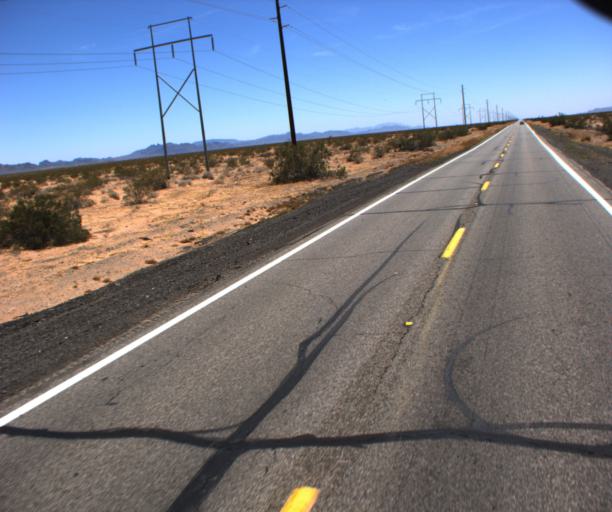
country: US
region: Arizona
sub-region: La Paz County
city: Quartzsite
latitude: 33.9048
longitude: -114.2169
